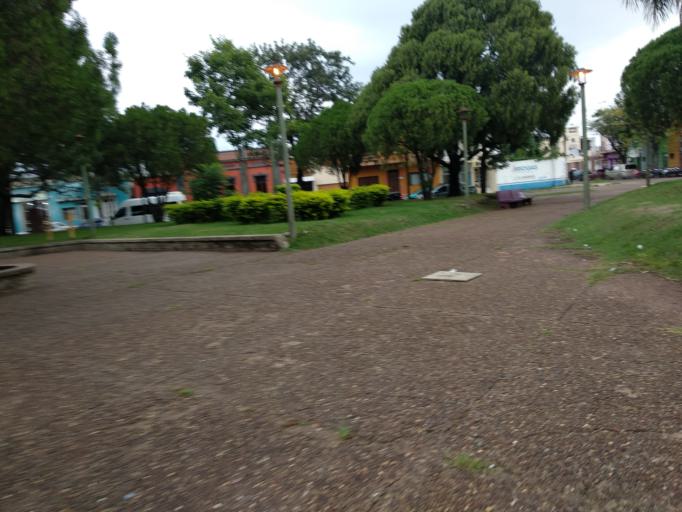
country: UY
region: Artigas
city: Artigas
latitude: -30.4038
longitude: -56.4697
